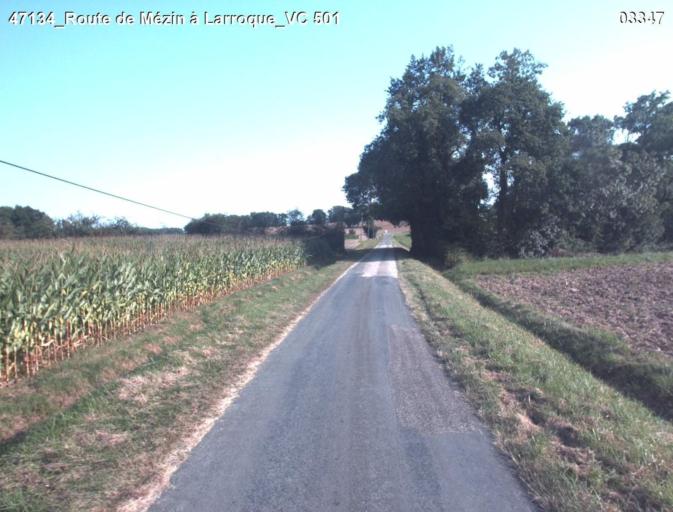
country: FR
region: Aquitaine
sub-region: Departement du Lot-et-Garonne
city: Mezin
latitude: 44.0249
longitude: 0.2698
